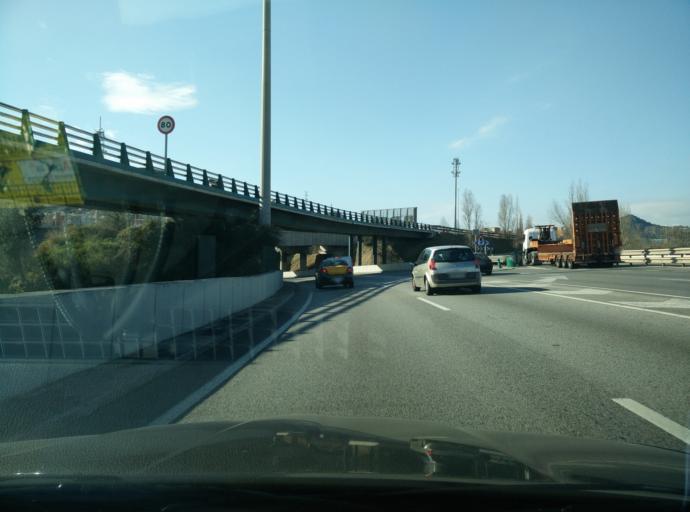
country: ES
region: Catalonia
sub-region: Provincia de Barcelona
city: Santa Coloma de Gramenet
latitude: 41.4505
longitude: 2.1969
